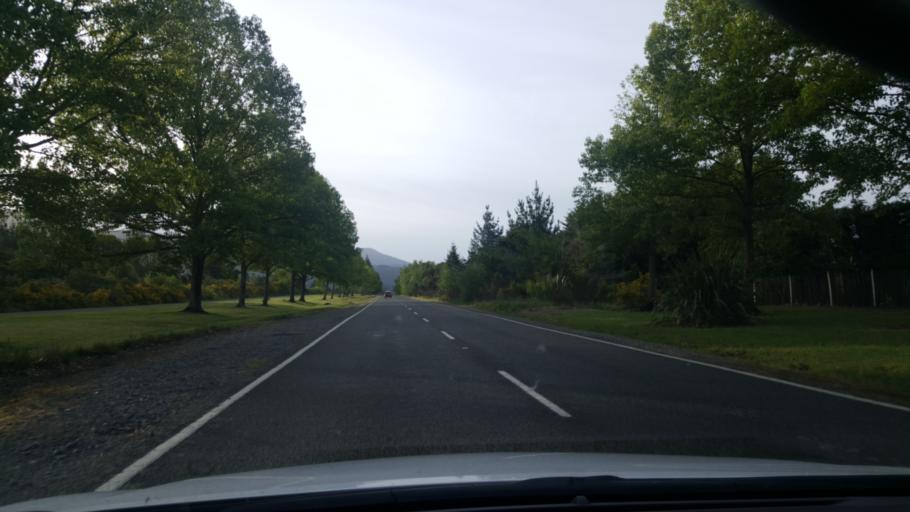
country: NZ
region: Waikato
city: Turangi
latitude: -38.9942
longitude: 175.7998
